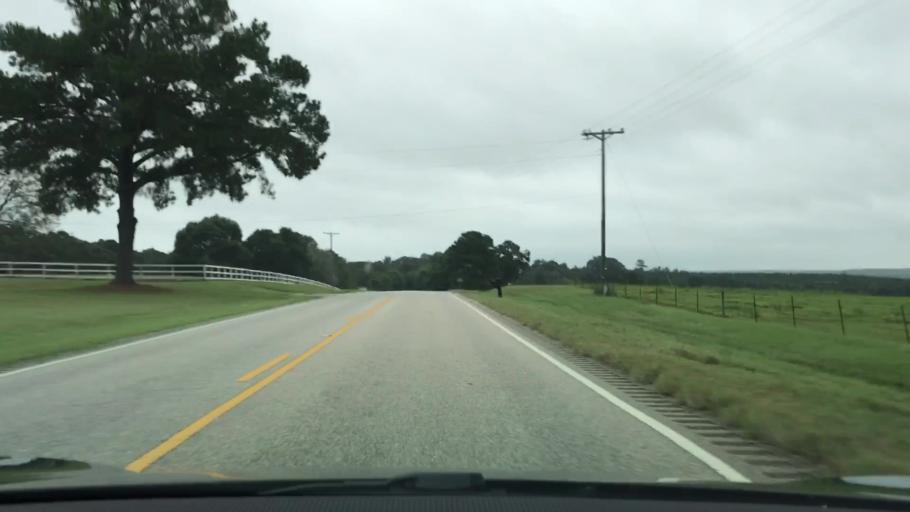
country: US
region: Alabama
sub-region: Coffee County
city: Elba
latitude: 31.3590
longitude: -86.1186
